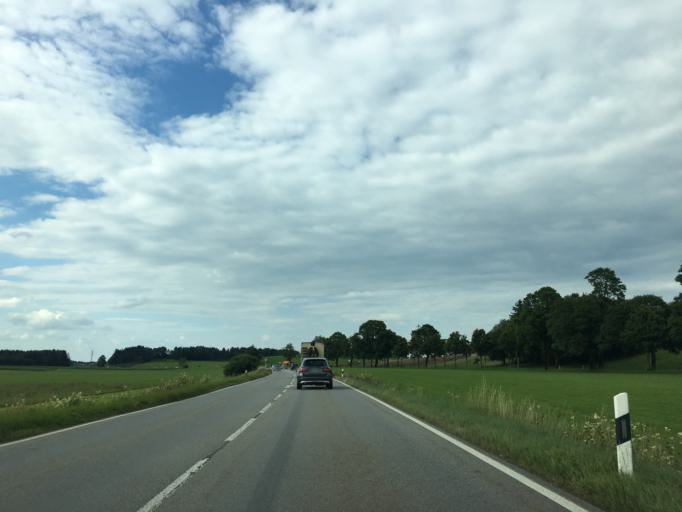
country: DE
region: Bavaria
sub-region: Upper Bavaria
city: Warngau
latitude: 47.8405
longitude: 11.7195
